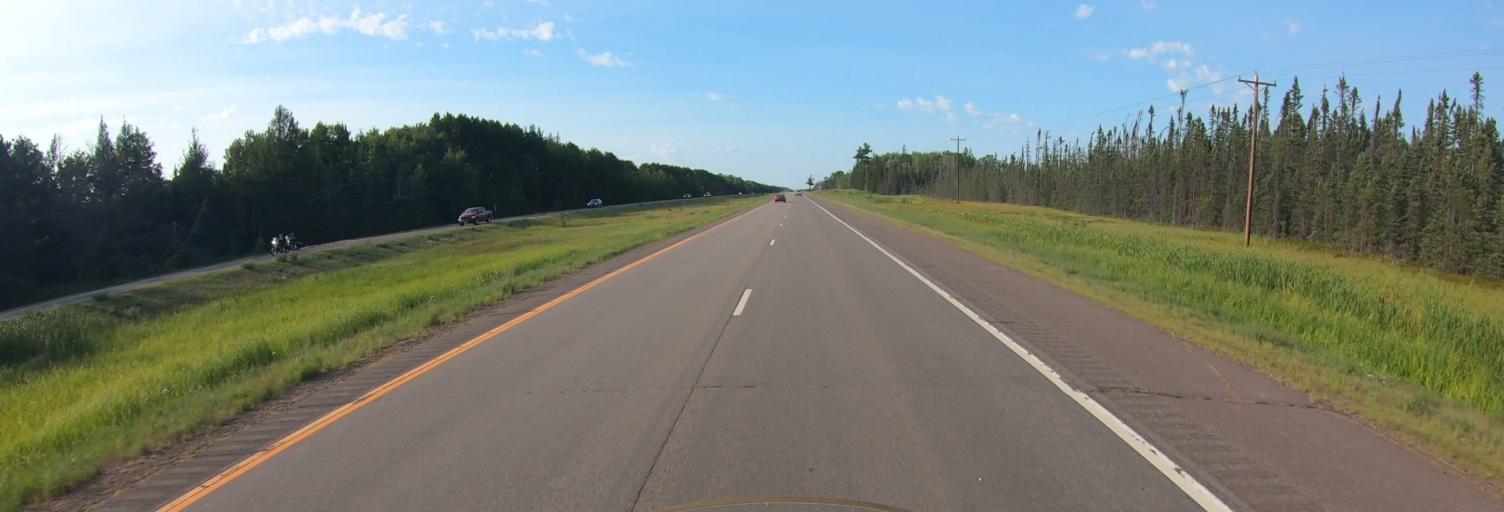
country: US
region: Minnesota
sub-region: Saint Louis County
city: Hermantown
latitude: 47.0967
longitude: -92.4714
